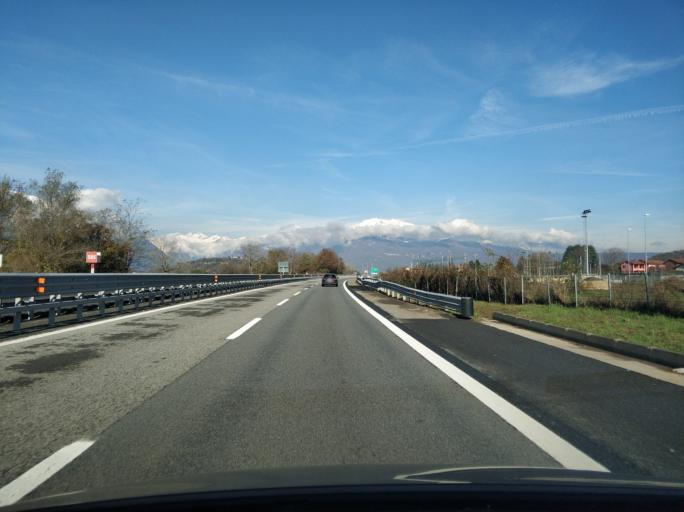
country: IT
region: Piedmont
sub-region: Provincia di Torino
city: Pavone Canavese
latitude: 45.4338
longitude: 7.8466
